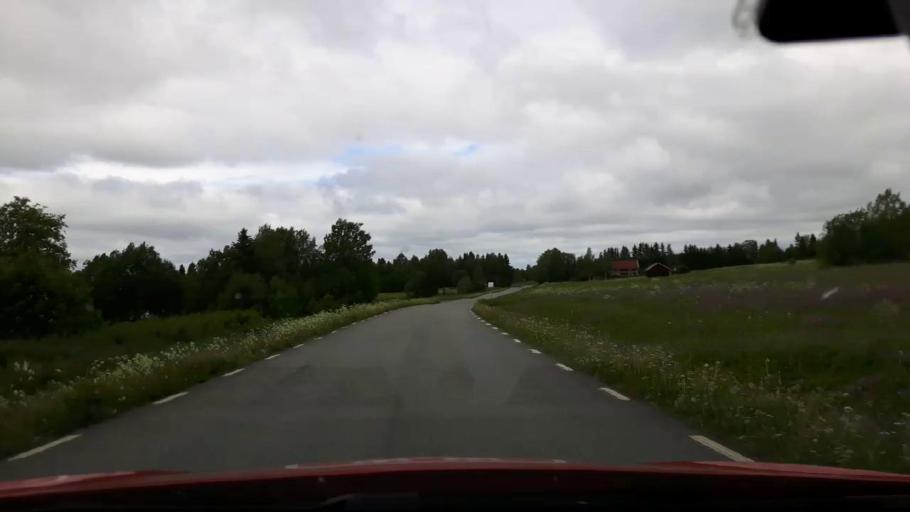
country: SE
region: Jaemtland
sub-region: Krokoms Kommun
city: Krokom
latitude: 63.2631
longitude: 14.5372
